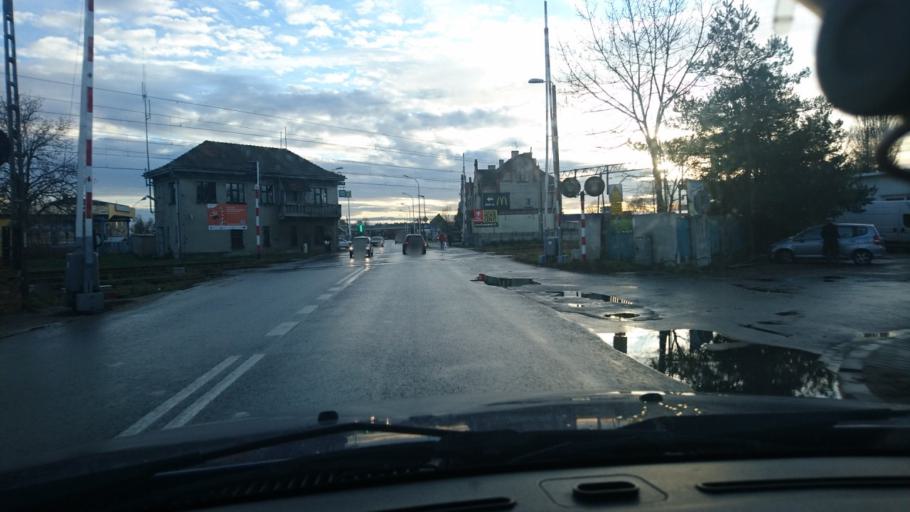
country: PL
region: Greater Poland Voivodeship
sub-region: Powiat kepinski
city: Kepno
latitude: 51.2904
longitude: 17.9942
